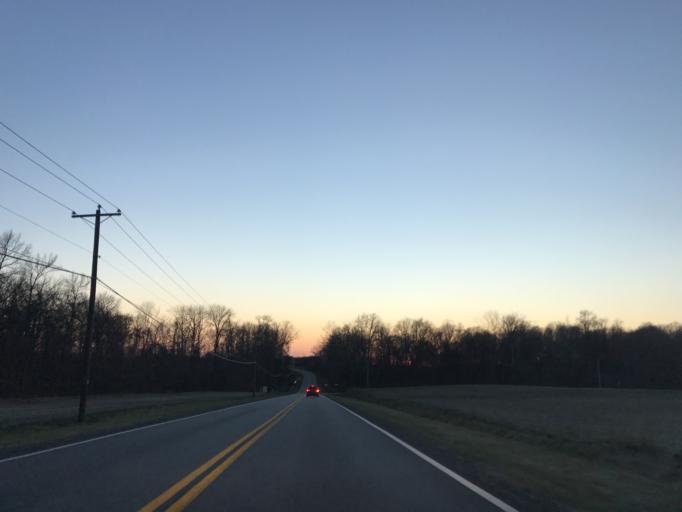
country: US
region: Maryland
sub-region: Queen Anne's County
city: Centreville
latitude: 39.0457
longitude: -76.0146
